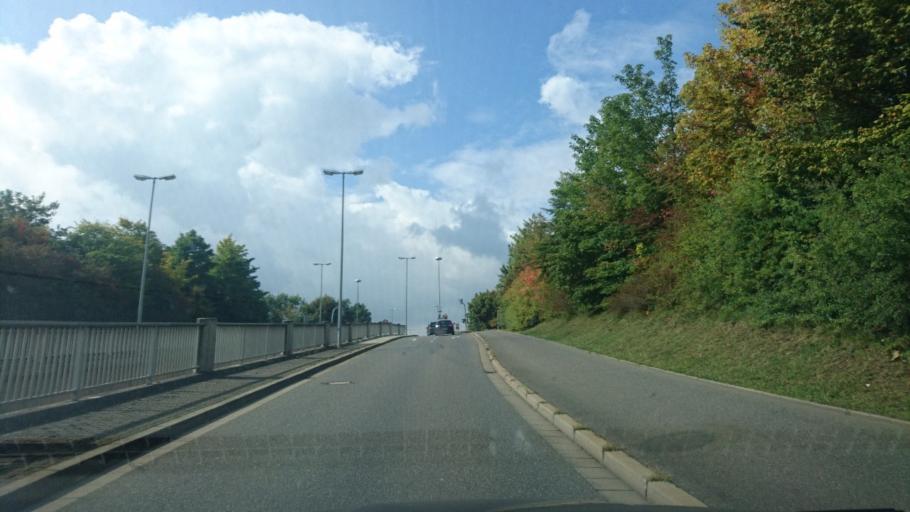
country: DE
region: Bavaria
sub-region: Upper Franconia
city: Bayreuth
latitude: 49.9587
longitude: 11.5902
